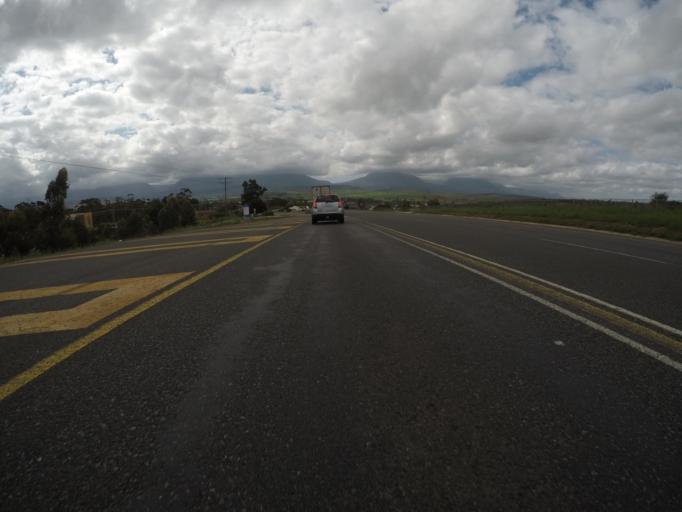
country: ZA
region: Western Cape
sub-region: Eden District Municipality
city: Riversdale
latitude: -34.0974
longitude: 21.2527
